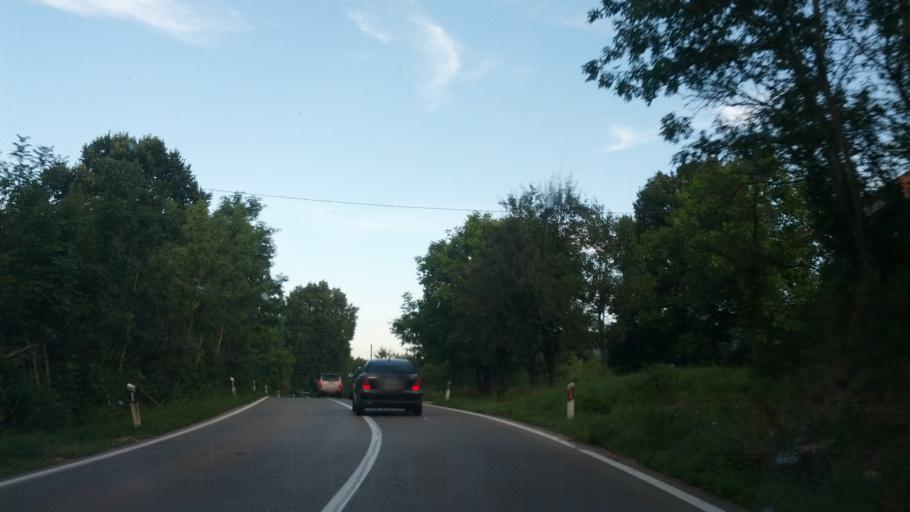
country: BA
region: Federation of Bosnia and Herzegovina
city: Izacic
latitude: 44.8890
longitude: 15.7252
